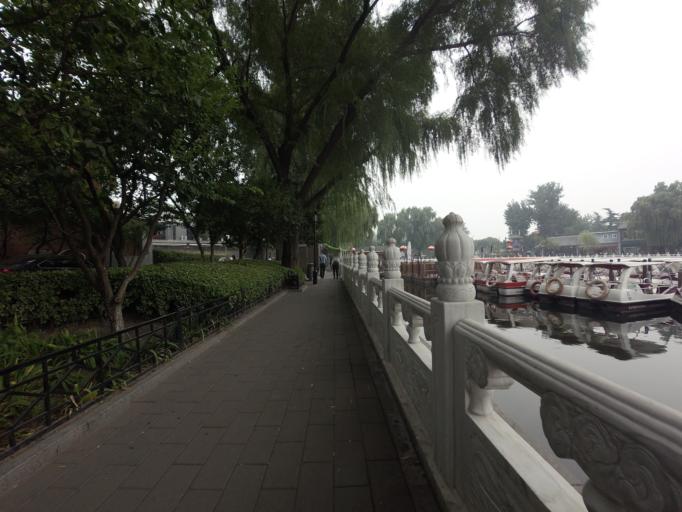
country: CN
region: Beijing
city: Jingshan
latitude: 39.9333
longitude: 116.3866
